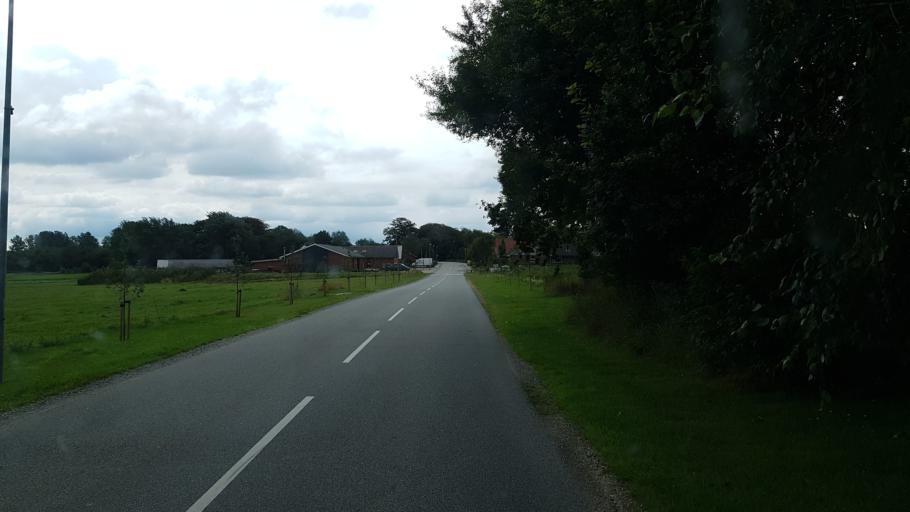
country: DK
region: South Denmark
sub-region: Varde Kommune
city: Varde
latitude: 55.7639
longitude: 8.4325
